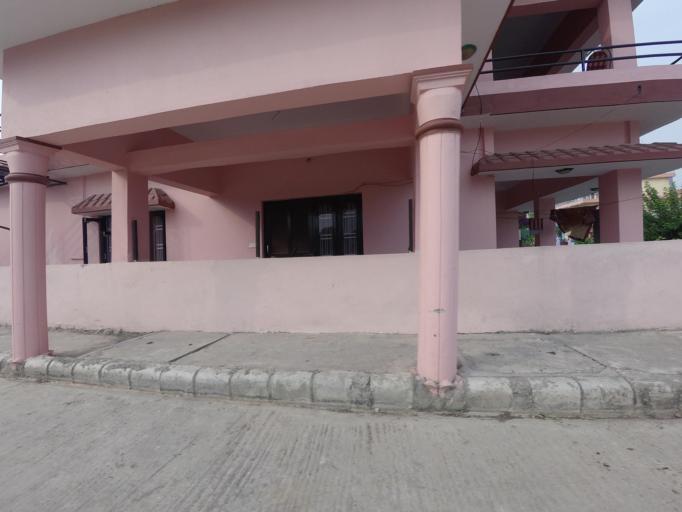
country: NP
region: Western Region
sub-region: Lumbini Zone
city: Bhairahawa
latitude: 27.5225
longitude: 83.4520
